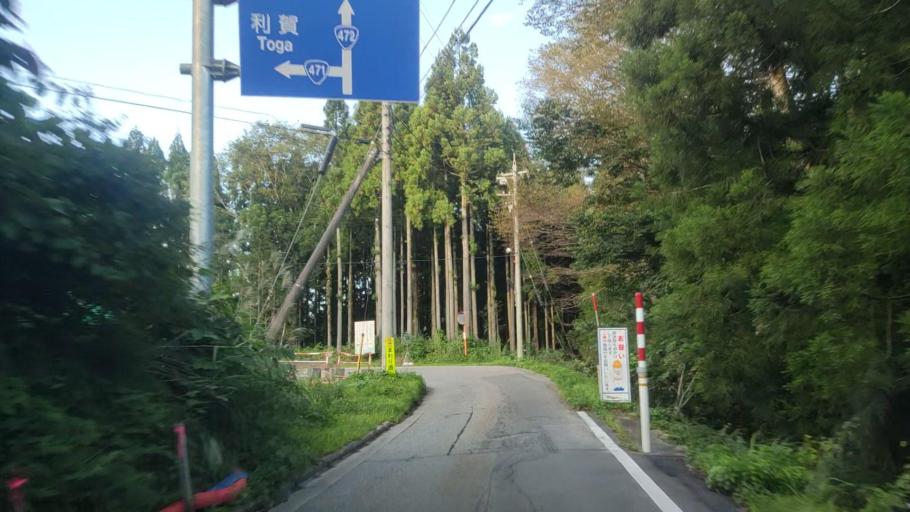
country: JP
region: Toyama
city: Yatsuomachi-higashikumisaka
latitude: 36.5048
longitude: 137.0647
